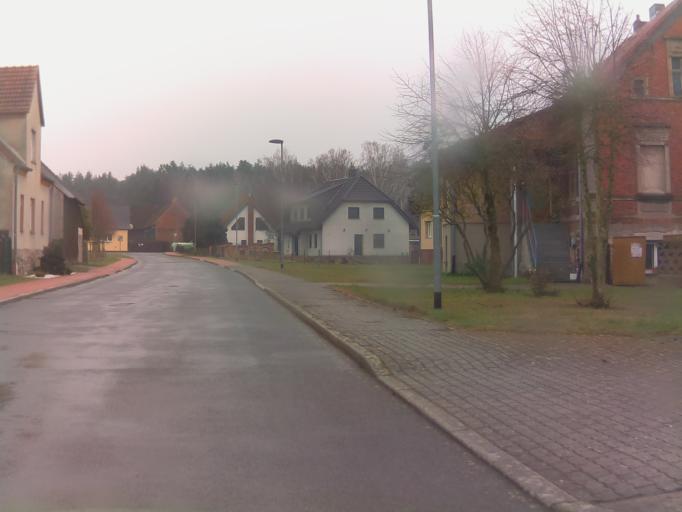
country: DE
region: Brandenburg
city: Jamlitz
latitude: 52.0390
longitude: 14.3675
